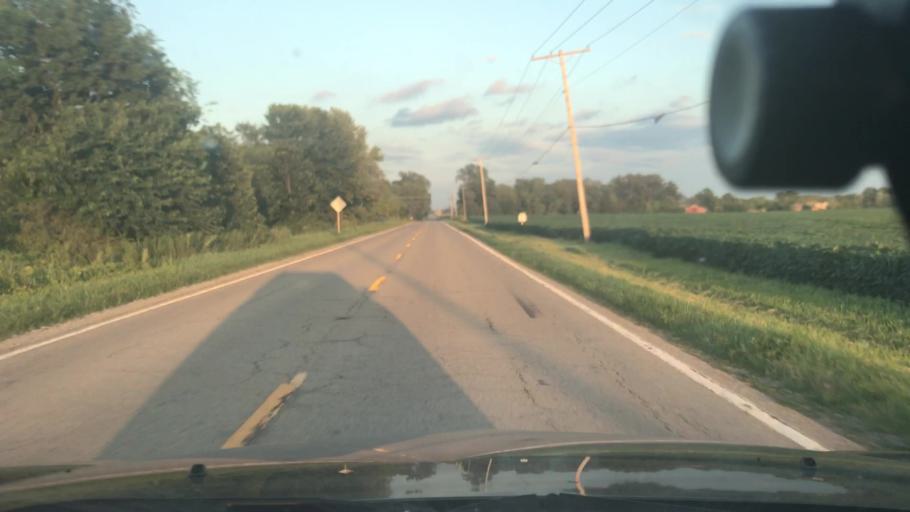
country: US
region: Illinois
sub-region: Washington County
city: Okawville
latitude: 38.4174
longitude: -89.5405
